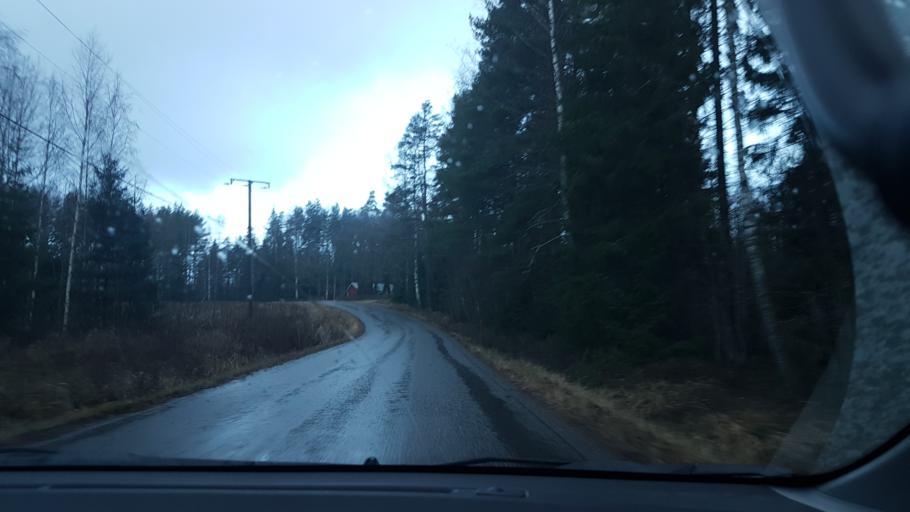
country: FI
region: Uusimaa
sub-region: Helsinki
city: Lohja
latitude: 60.2146
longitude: 24.0954
